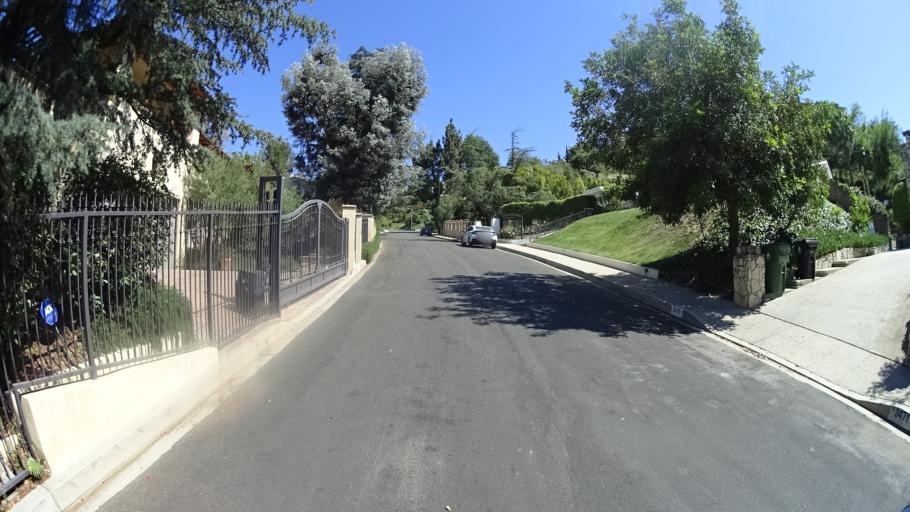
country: US
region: California
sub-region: Los Angeles County
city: Sherman Oaks
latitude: 34.1341
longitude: -118.4891
